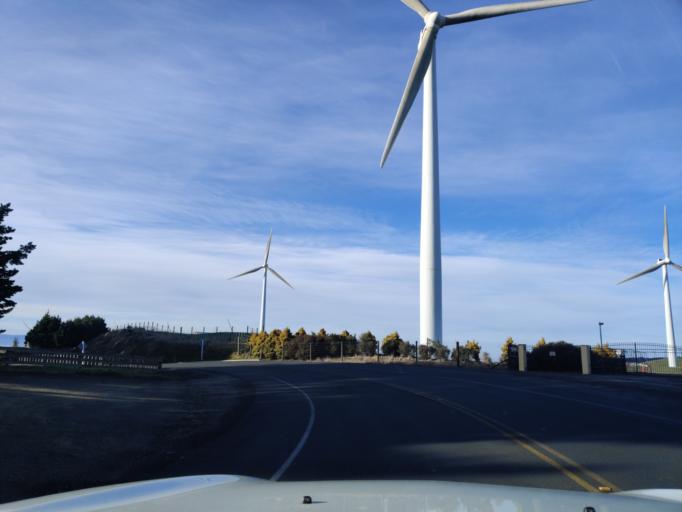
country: NZ
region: Manawatu-Wanganui
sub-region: Palmerston North City
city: Palmerston North
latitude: -40.2942
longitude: 175.8046
